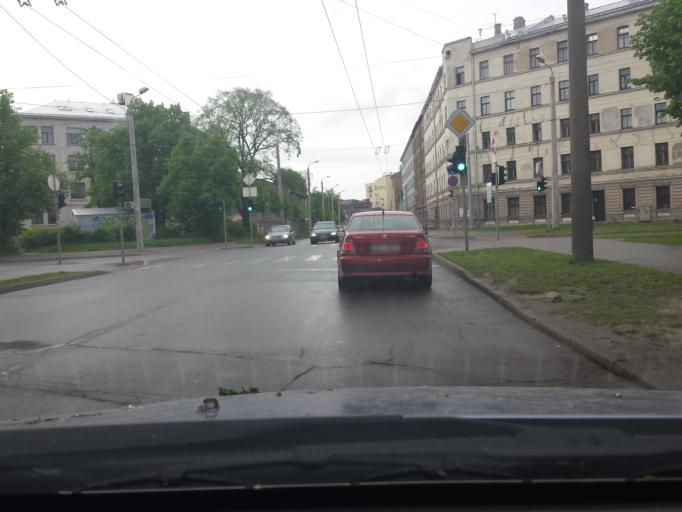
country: LV
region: Riga
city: Riga
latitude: 56.9615
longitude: 24.1515
